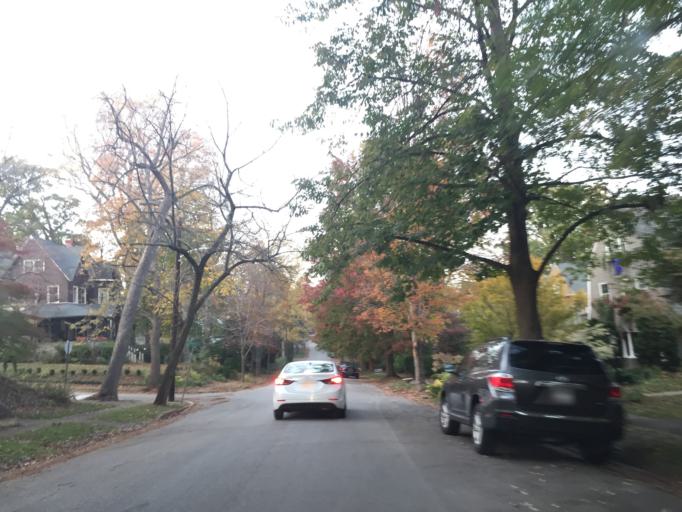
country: US
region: Maryland
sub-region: Baltimore County
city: Towson
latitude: 39.3509
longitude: -76.6319
